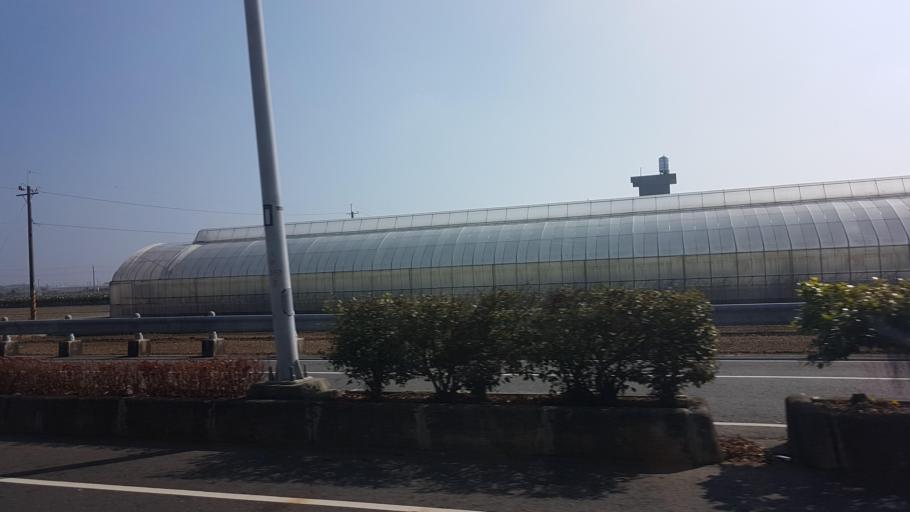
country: TW
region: Taiwan
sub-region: Chiayi
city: Taibao
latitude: 23.4364
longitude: 120.3228
